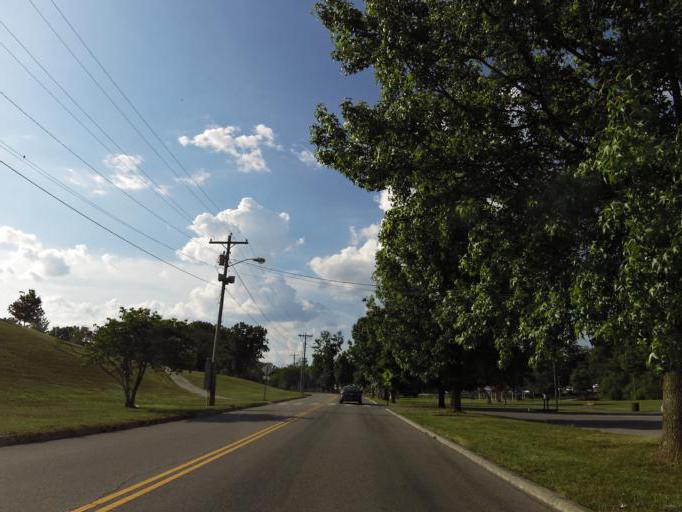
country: US
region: Tennessee
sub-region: Blount County
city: Alcoa
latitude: 35.7911
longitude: -83.9769
